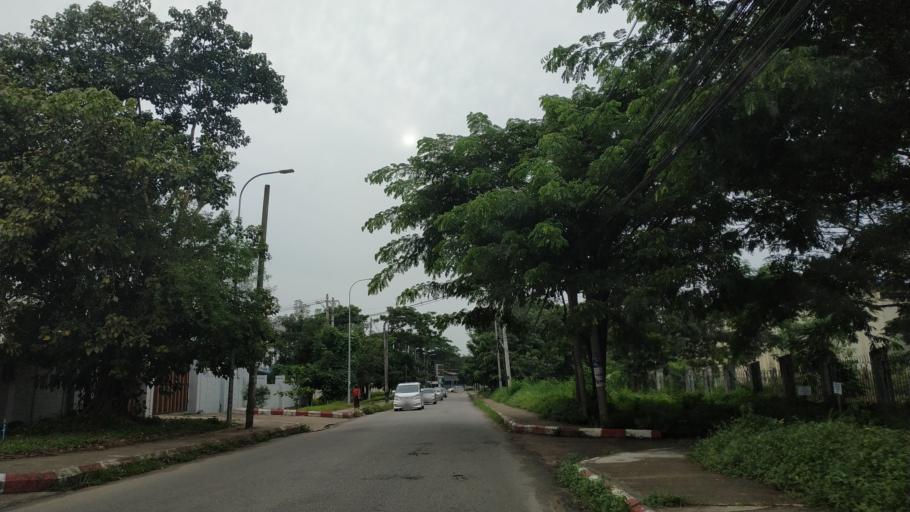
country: MM
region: Yangon
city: Yangon
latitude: 16.8483
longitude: 96.1321
